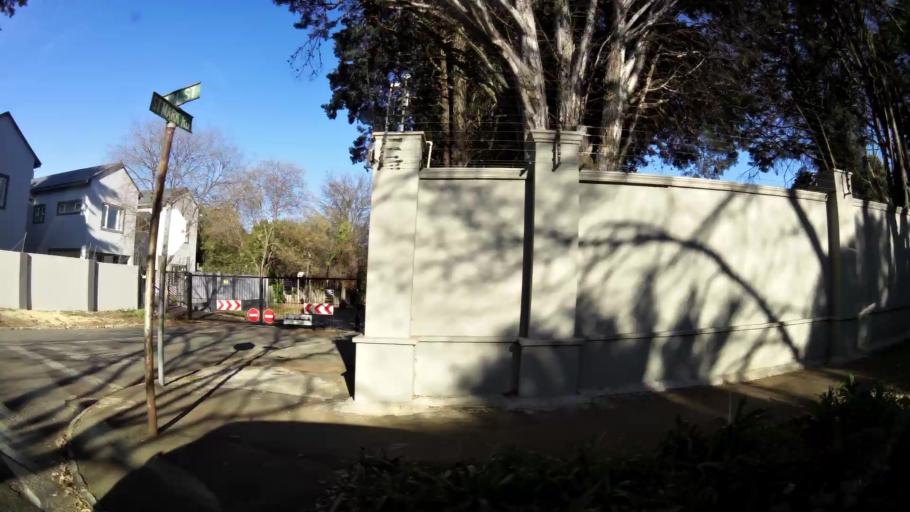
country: ZA
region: Gauteng
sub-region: City of Johannesburg Metropolitan Municipality
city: Johannesburg
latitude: -26.1746
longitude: 28.0605
